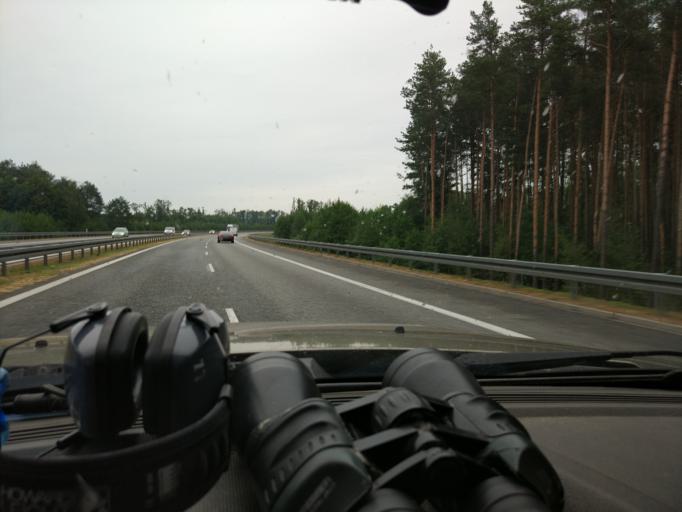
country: PL
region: Masovian Voivodeship
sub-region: Powiat wyszkowski
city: Wyszkow
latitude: 52.5658
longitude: 21.4684
